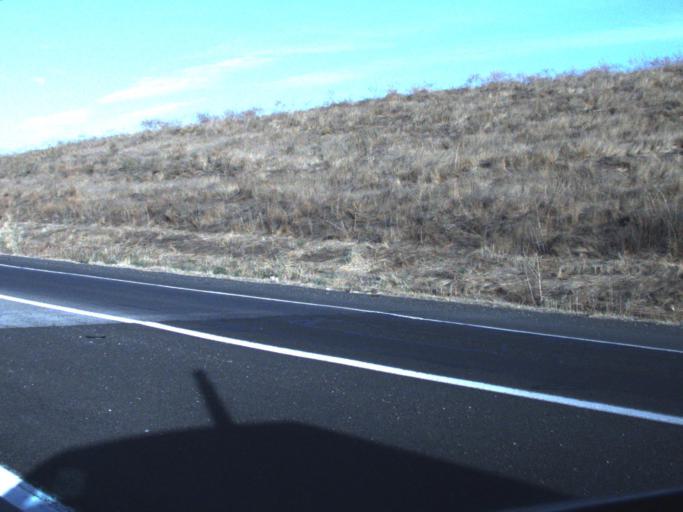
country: US
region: Washington
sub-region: Yakima County
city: Sunnyside
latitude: 46.3064
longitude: -119.9845
